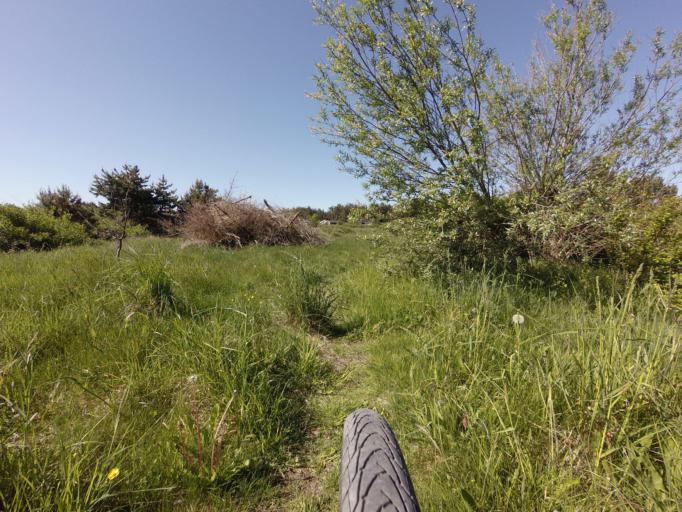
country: DK
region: North Denmark
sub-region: Jammerbugt Kommune
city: Pandrup
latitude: 57.3178
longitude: 9.6681
